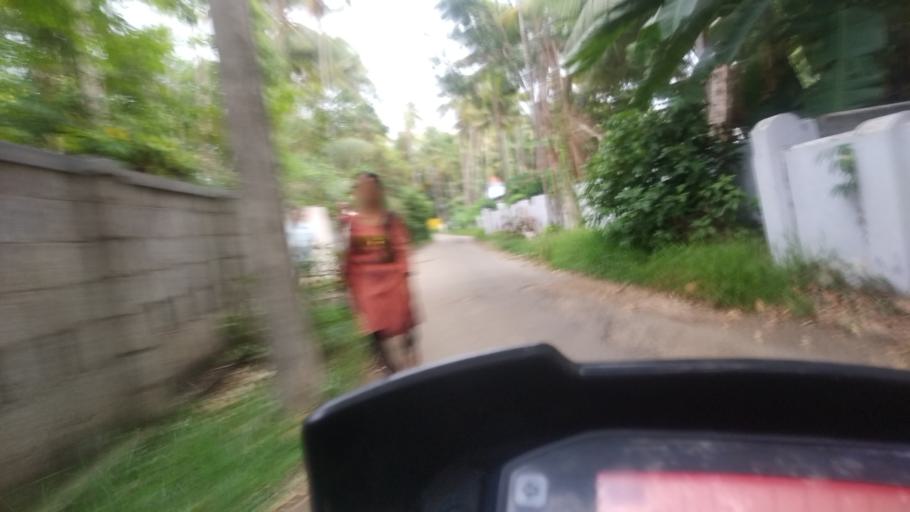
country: IN
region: Kerala
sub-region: Ernakulam
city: Elur
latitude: 10.0690
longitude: 76.2219
